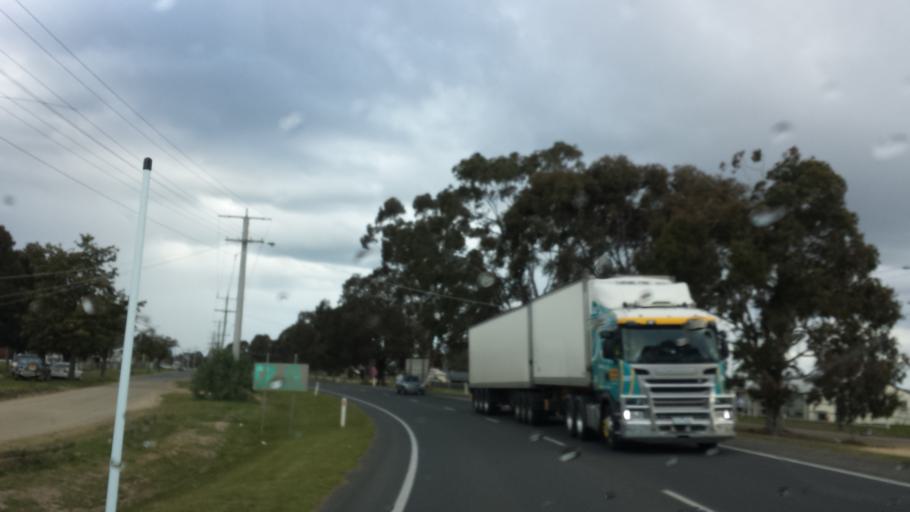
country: AU
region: Victoria
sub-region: East Gippsland
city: Bairnsdale
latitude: -37.8111
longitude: 147.6473
